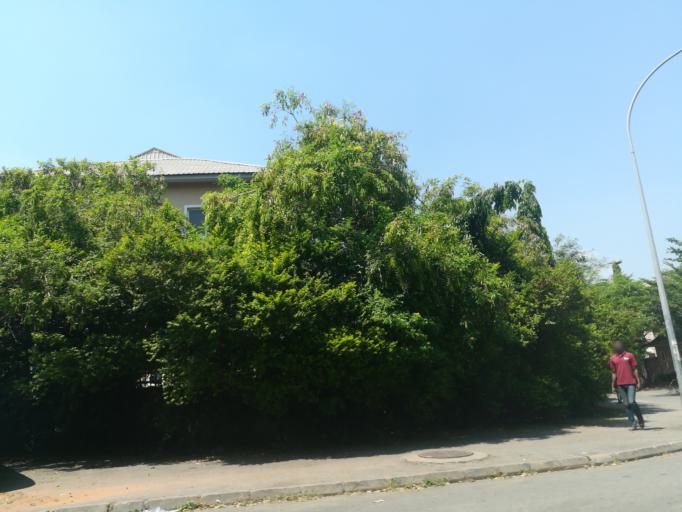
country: NG
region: Abuja Federal Capital Territory
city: Abuja
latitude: 9.0749
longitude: 7.4493
